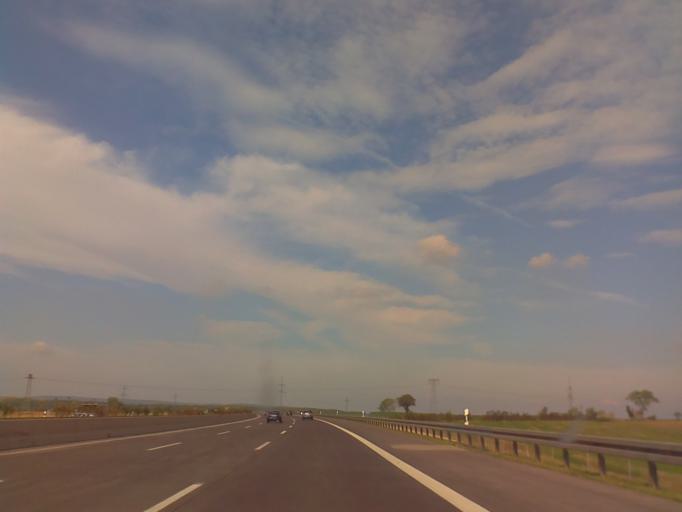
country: DE
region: Thuringia
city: Haina
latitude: 50.9639
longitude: 10.4884
